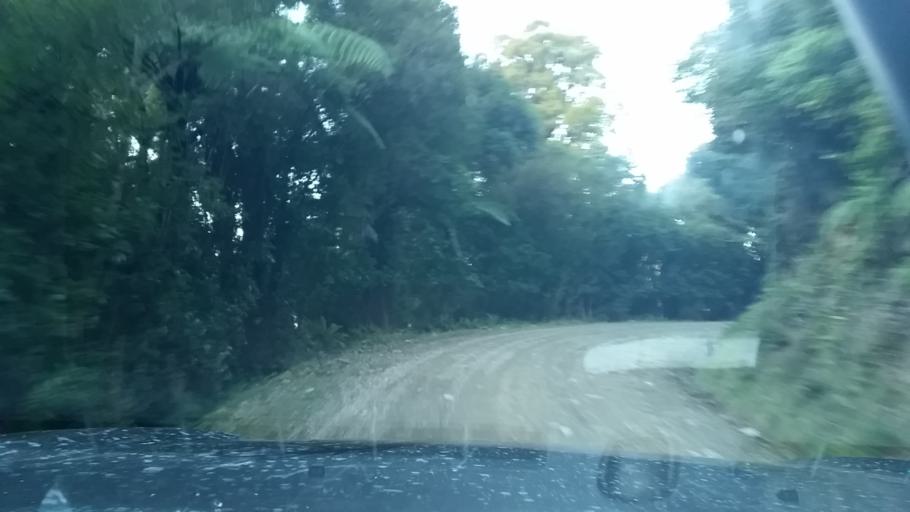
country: NZ
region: Marlborough
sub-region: Marlborough District
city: Picton
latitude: -41.0812
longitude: 174.1197
